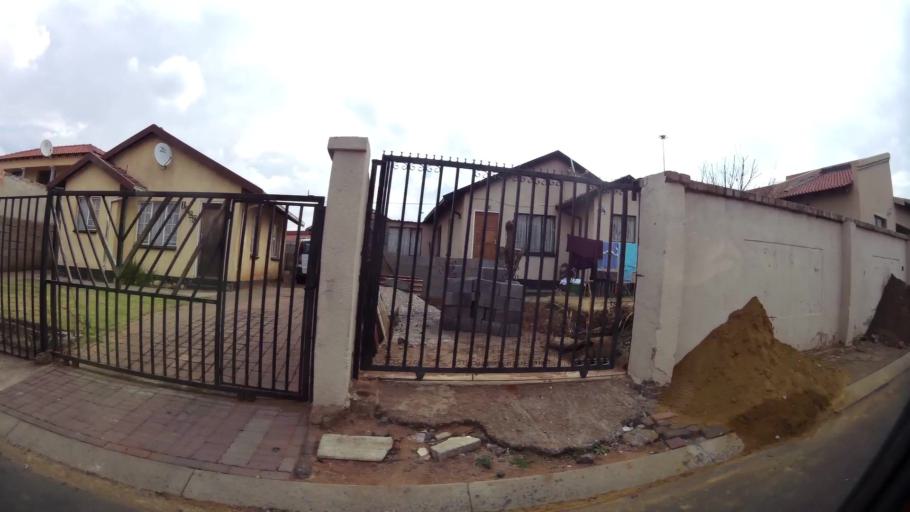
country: ZA
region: Gauteng
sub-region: City of Johannesburg Metropolitan Municipality
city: Soweto
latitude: -26.2361
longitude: 27.8707
